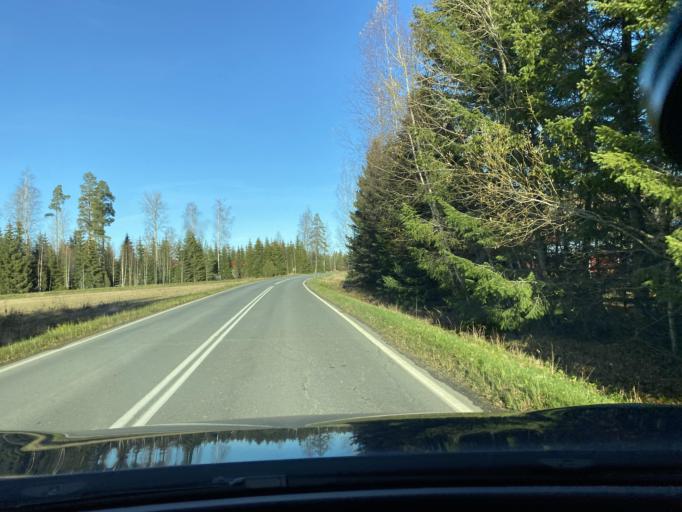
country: FI
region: Haeme
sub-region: Forssa
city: Tammela
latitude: 60.8465
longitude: 23.8375
